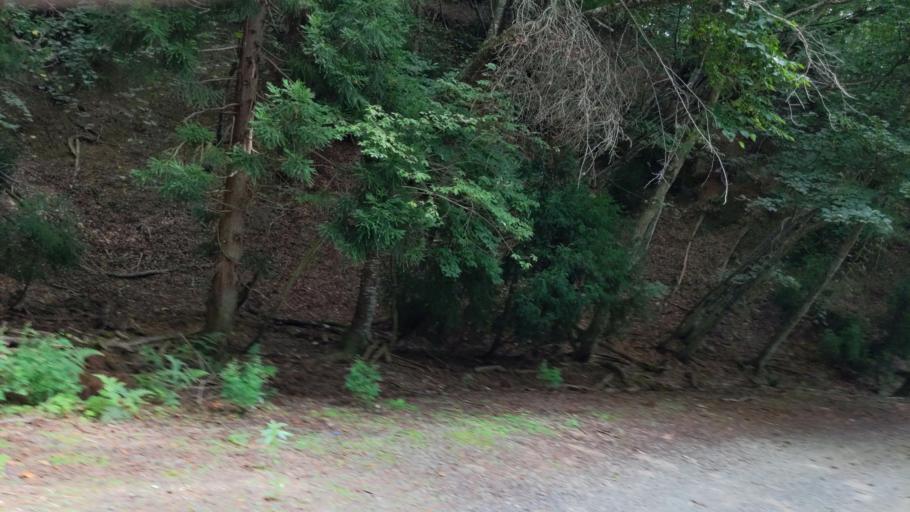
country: JP
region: Kyoto
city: Maizuru
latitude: 35.3918
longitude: 135.4404
